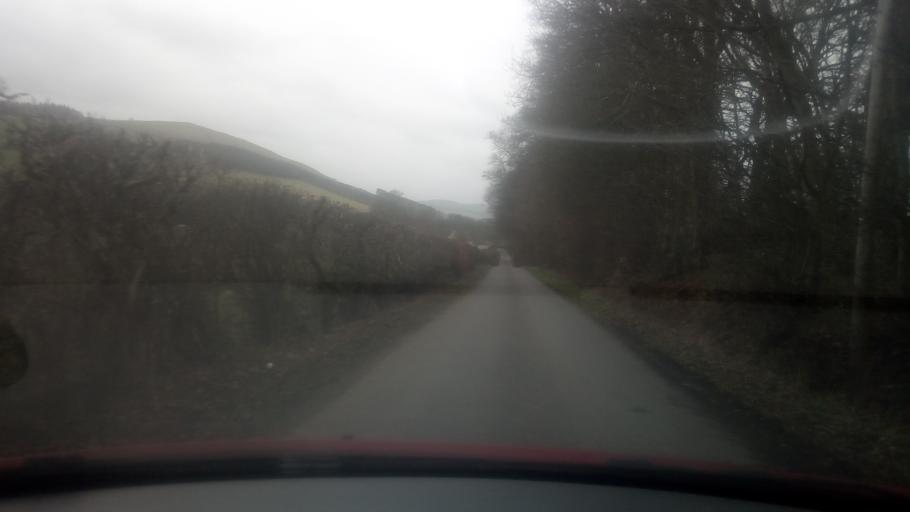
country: GB
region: Scotland
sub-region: The Scottish Borders
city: Jedburgh
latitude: 55.4140
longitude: -2.6473
